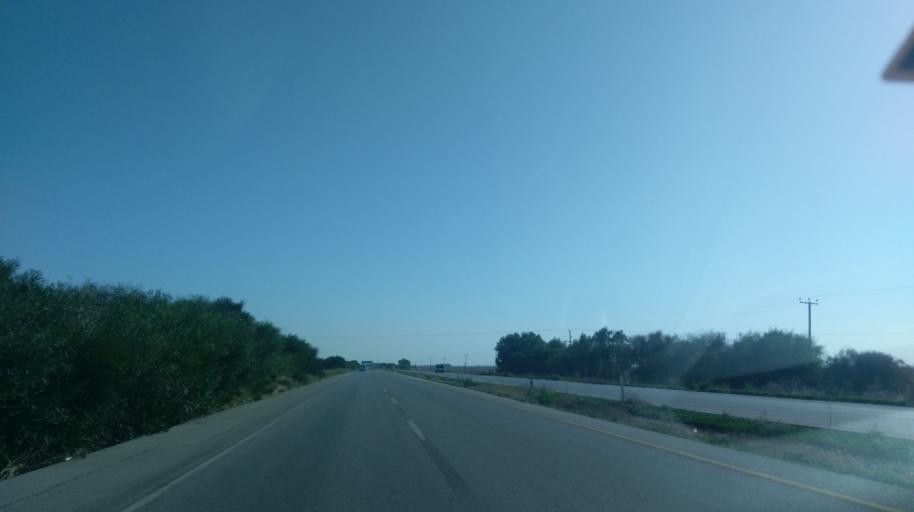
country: CY
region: Ammochostos
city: Lefkonoiko
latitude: 35.1836
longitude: 33.6899
